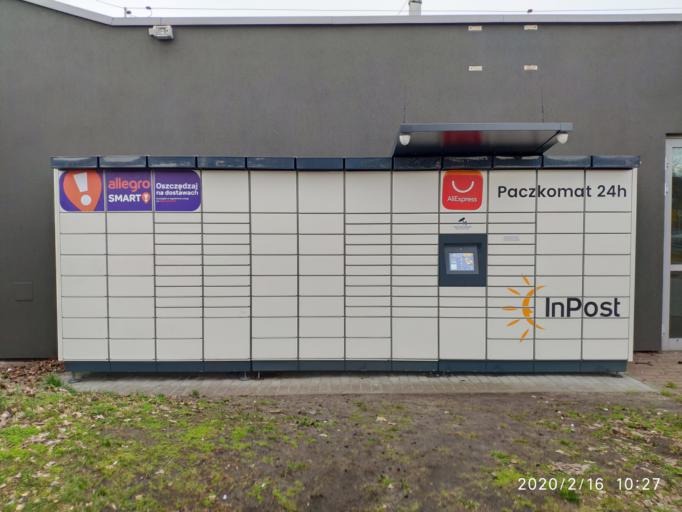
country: PL
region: Lubusz
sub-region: Zielona Gora
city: Zielona Gora
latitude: 51.9368
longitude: 15.5113
